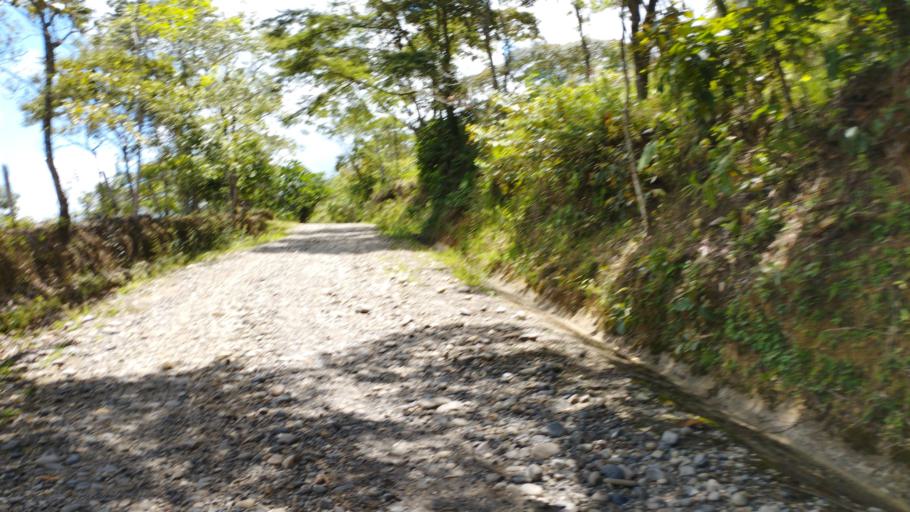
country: CO
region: Boyaca
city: San Luis de Gaceno
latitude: 4.7518
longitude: -73.1392
